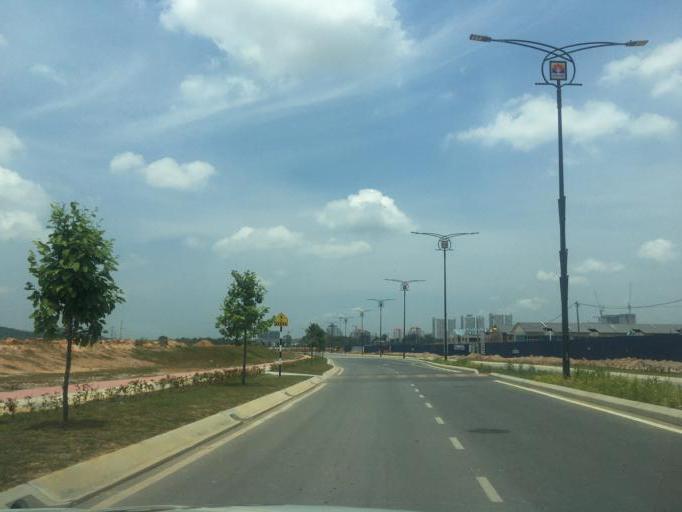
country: MY
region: Putrajaya
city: Putrajaya
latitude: 2.8520
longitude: 101.7052
